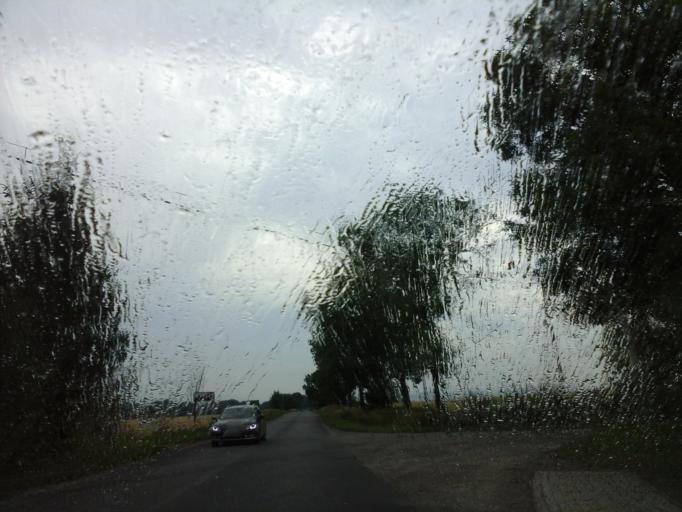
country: PL
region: Lower Silesian Voivodeship
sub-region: Powiat zabkowicki
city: Zabkowice Slaskie
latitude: 50.6155
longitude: 16.8445
